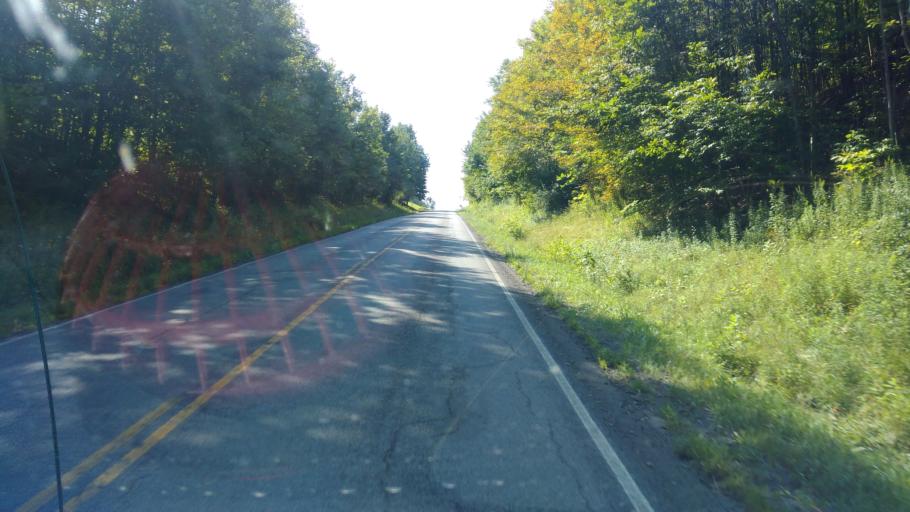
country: US
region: New York
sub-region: Allegany County
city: Friendship
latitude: 42.1637
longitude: -78.1492
